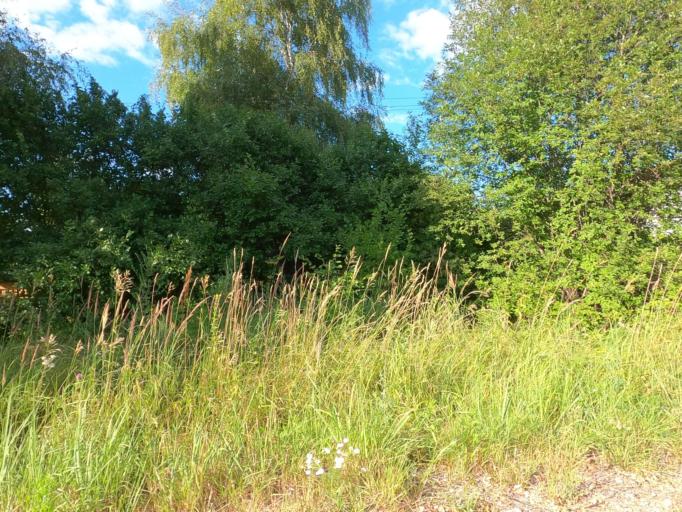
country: RU
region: Moskovskaya
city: Konobeyevo
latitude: 55.4124
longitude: 38.7214
